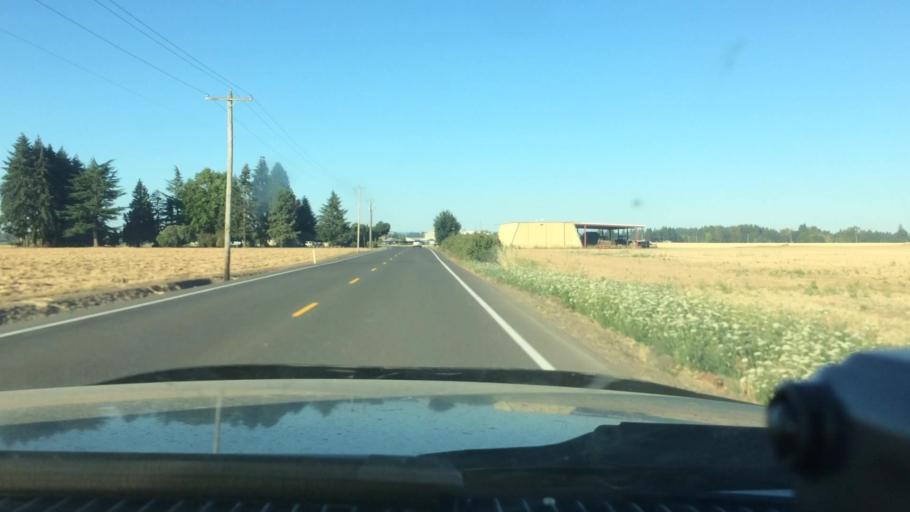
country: US
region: Oregon
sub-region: Yamhill County
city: Dundee
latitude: 45.2342
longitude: -122.9630
